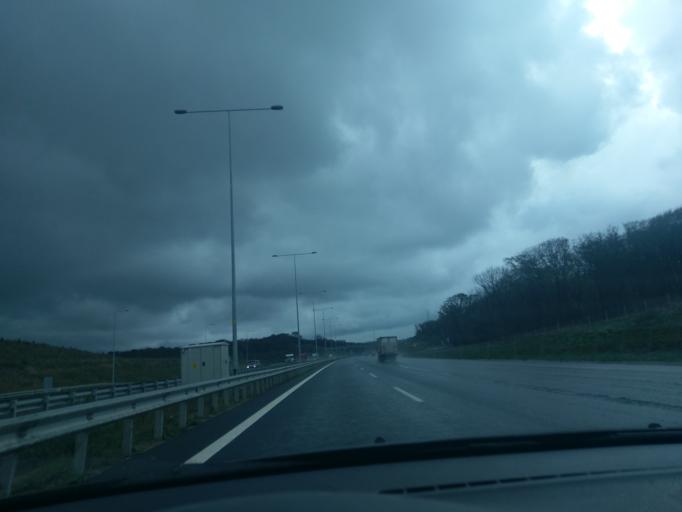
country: TR
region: Istanbul
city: Kemerburgaz
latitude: 41.2352
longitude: 28.9109
